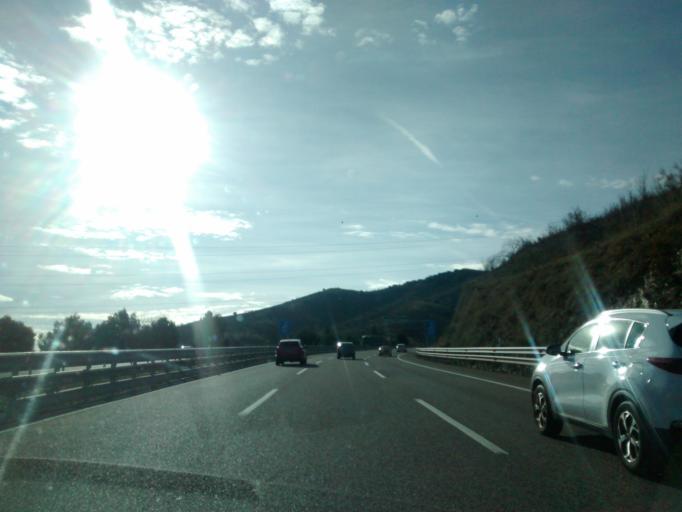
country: ES
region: Aragon
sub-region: Provincia de Zaragoza
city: Morata de Jalon
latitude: 41.4403
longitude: -1.4805
